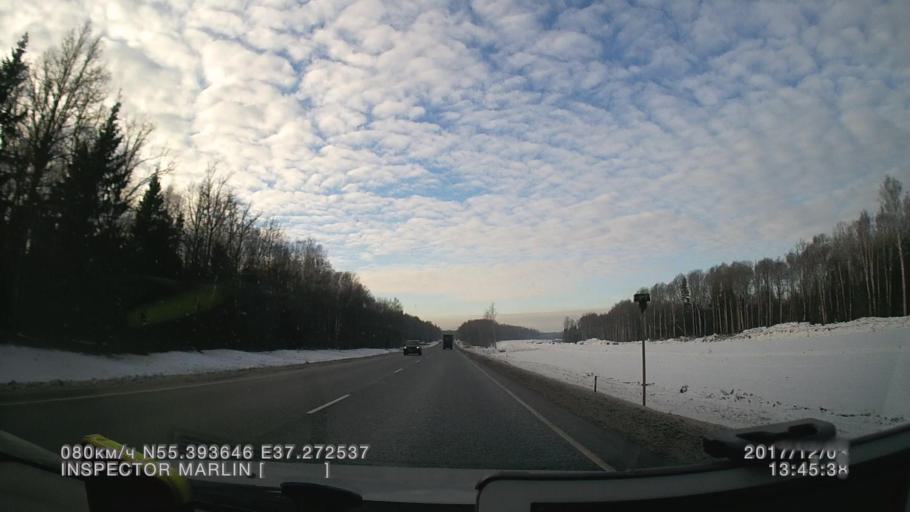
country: RU
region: Moskovskaya
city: Troitsk
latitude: 55.3936
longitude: 37.2727
